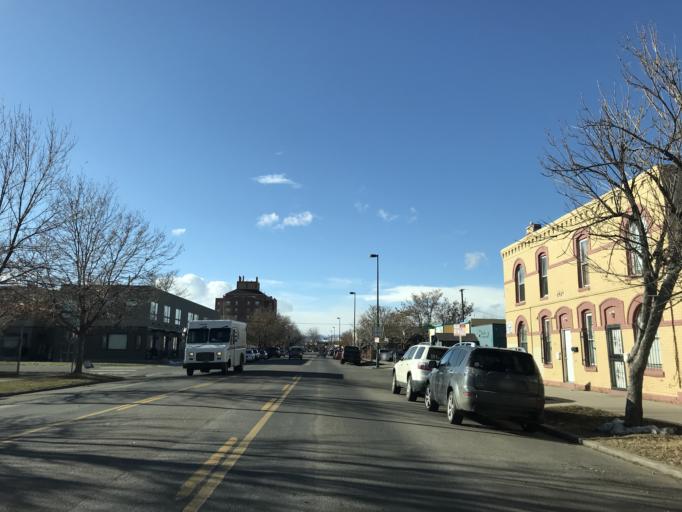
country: US
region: Colorado
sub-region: Denver County
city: Denver
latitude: 39.7647
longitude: -104.9689
